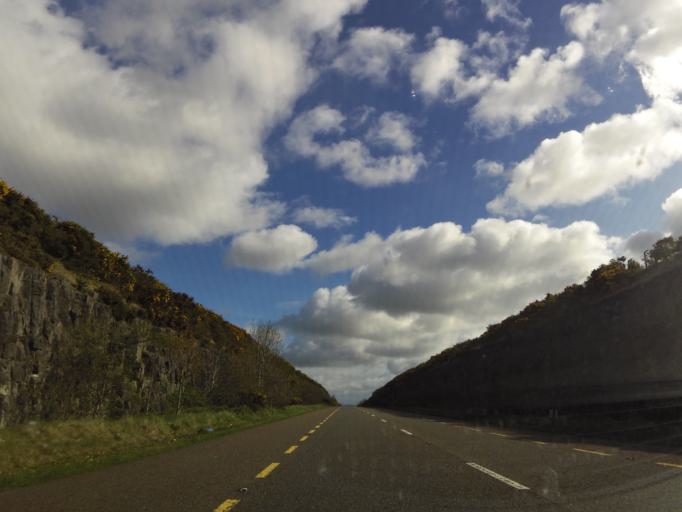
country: IE
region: Connaught
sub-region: Maigh Eo
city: Kiltamagh
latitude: 53.7892
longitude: -8.9355
